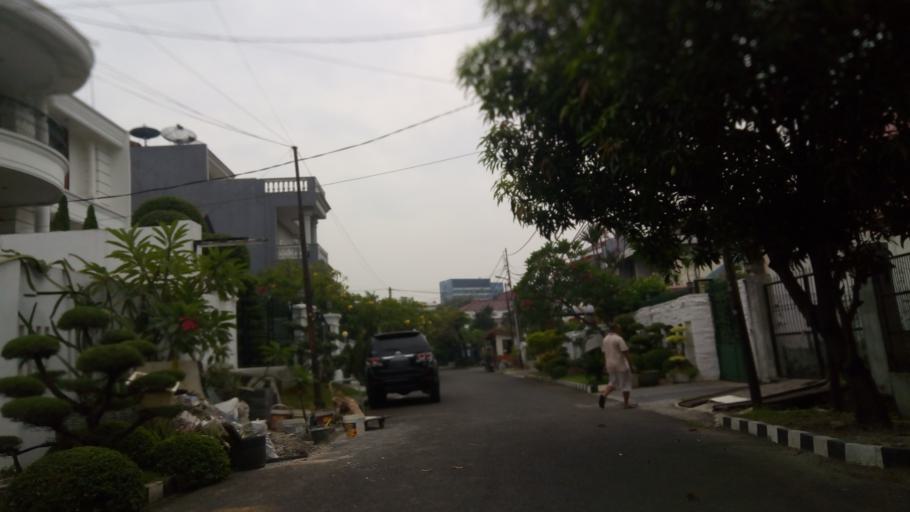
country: ID
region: Jakarta Raya
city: Jakarta
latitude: -6.1458
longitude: 106.8421
